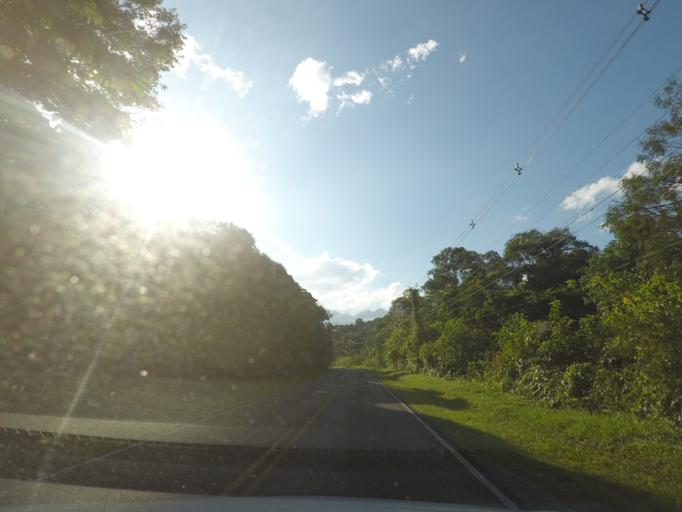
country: BR
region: Parana
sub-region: Antonina
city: Antonina
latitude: -25.4290
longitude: -48.8747
